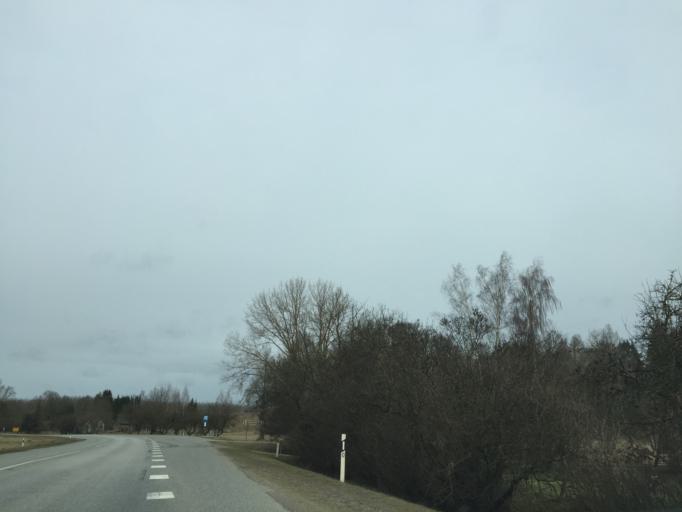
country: LV
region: Jekabpils Rajons
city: Jekabpils
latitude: 56.4912
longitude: 25.9162
